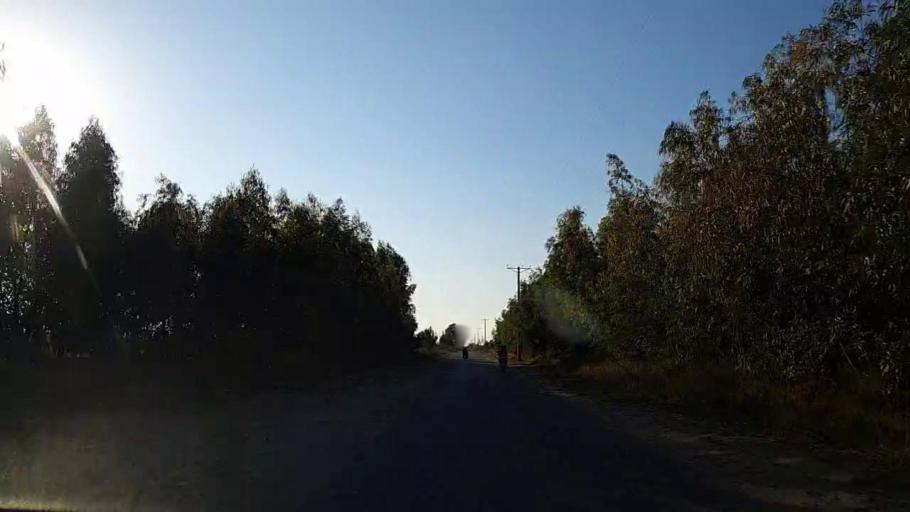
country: PK
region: Sindh
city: Khadro
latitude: 26.2790
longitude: 68.8984
